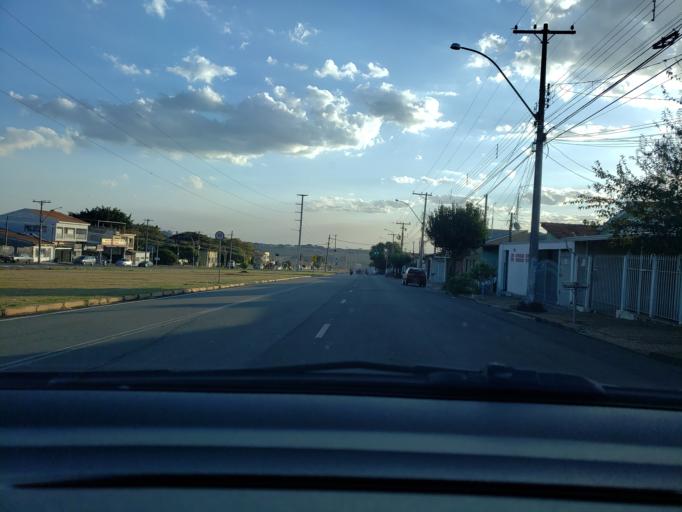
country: BR
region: Sao Paulo
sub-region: Santa Barbara D'Oeste
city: Santa Barbara d'Oeste
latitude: -22.7399
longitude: -47.3777
